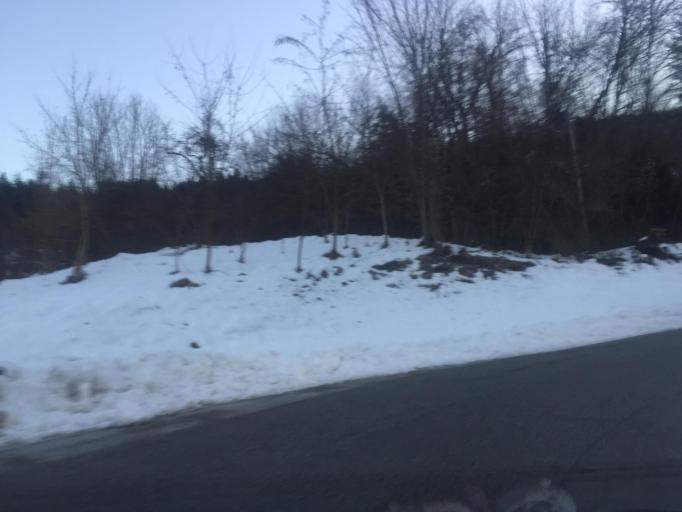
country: IT
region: Friuli Venezia Giulia
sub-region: Provincia di Udine
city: Villa Santina
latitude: 46.4225
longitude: 12.9169
